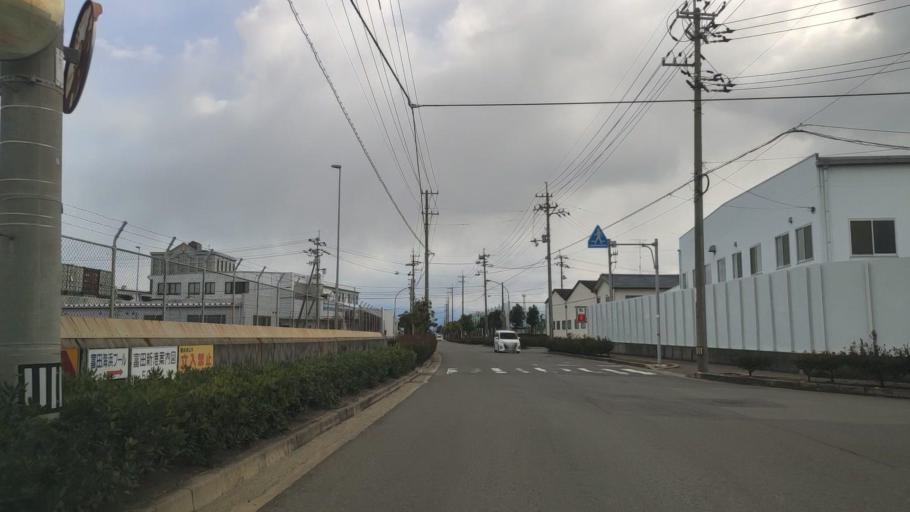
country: JP
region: Ehime
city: Saijo
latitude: 34.0499
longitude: 133.0251
